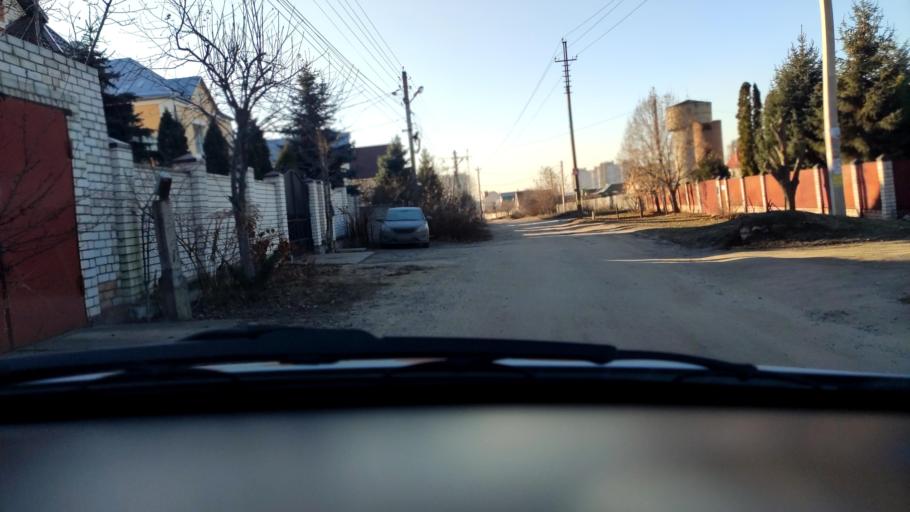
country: RU
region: Voronezj
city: Podgornoye
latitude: 51.7242
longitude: 39.1527
